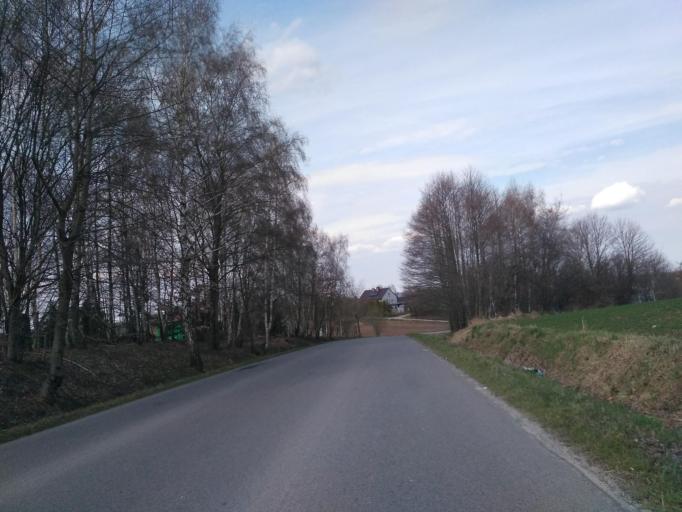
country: PL
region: Subcarpathian Voivodeship
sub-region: Powiat ropczycko-sedziszowski
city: Iwierzyce
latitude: 50.0007
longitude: 21.7960
